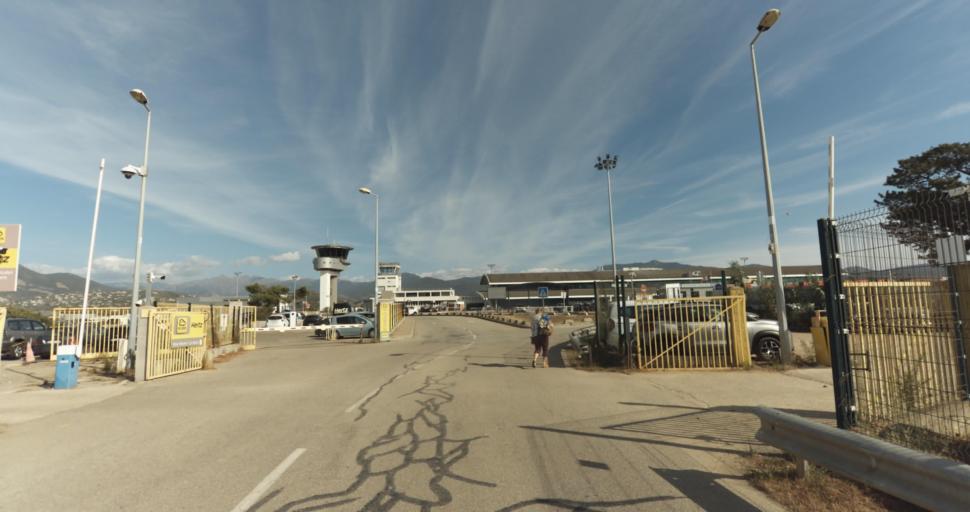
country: FR
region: Corsica
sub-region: Departement de la Corse-du-Sud
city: Ajaccio
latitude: 41.9209
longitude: 8.7927
